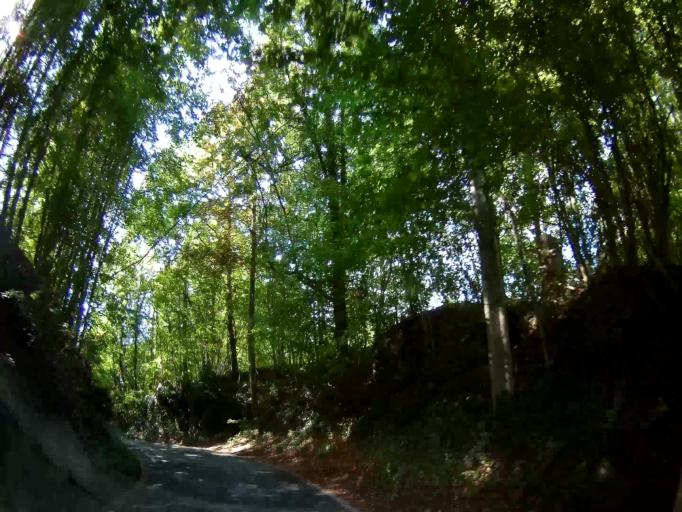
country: BE
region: Wallonia
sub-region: Province de Namur
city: Onhaye
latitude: 50.2962
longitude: 4.7764
